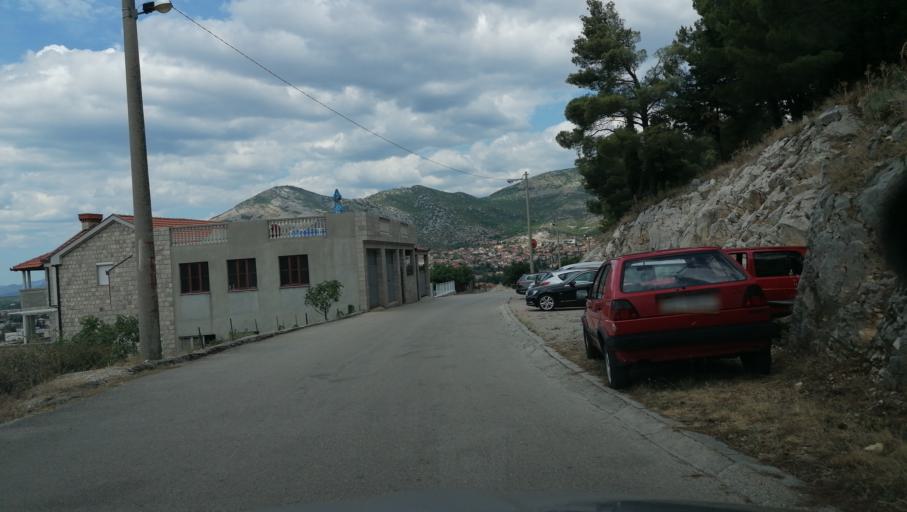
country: BA
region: Republika Srpska
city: Trebinje
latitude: 42.7082
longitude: 18.3593
